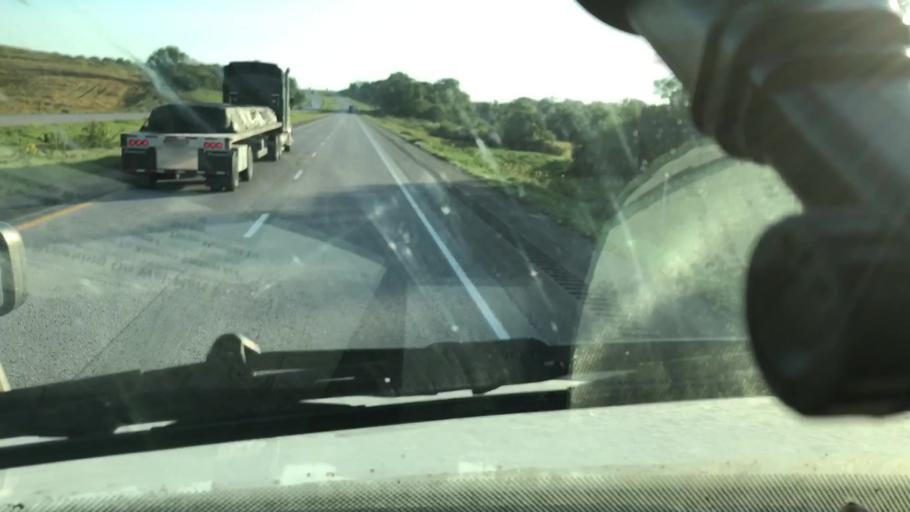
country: US
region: Iowa
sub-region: Pottawattamie County
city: Council Bluffs
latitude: 41.3334
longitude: -95.7395
